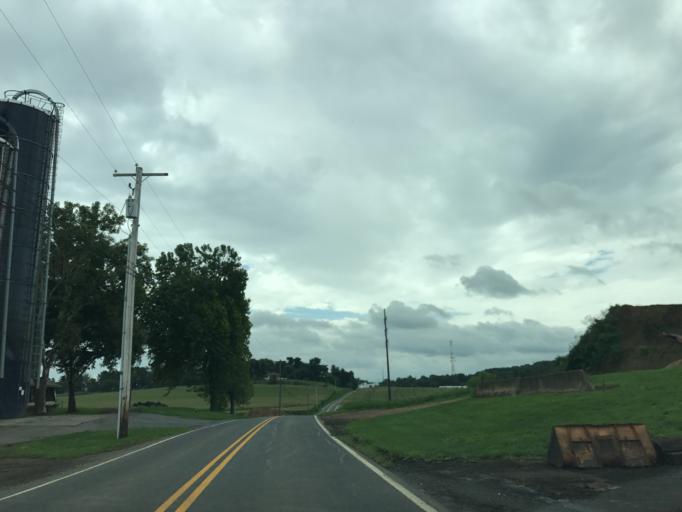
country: US
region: Pennsylvania
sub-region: Lancaster County
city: East Petersburg
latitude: 40.0910
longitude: -76.3741
